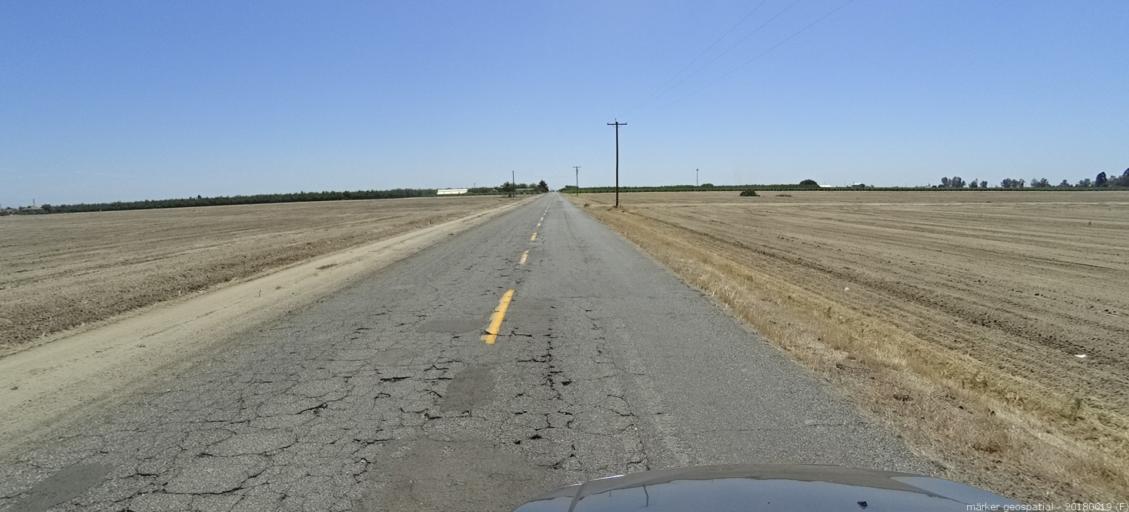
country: US
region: California
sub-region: Fresno County
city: Biola
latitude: 36.8368
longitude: -120.0688
